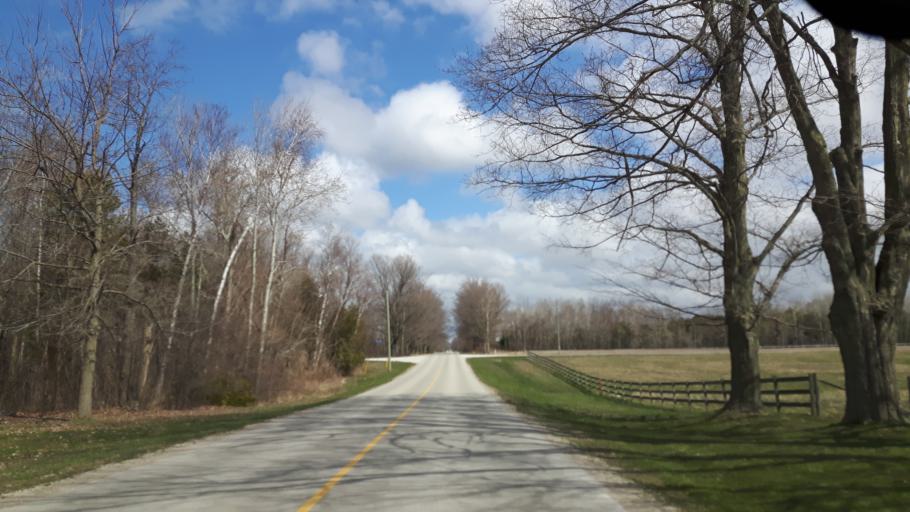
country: CA
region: Ontario
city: Goderich
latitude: 43.6230
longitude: -81.6846
